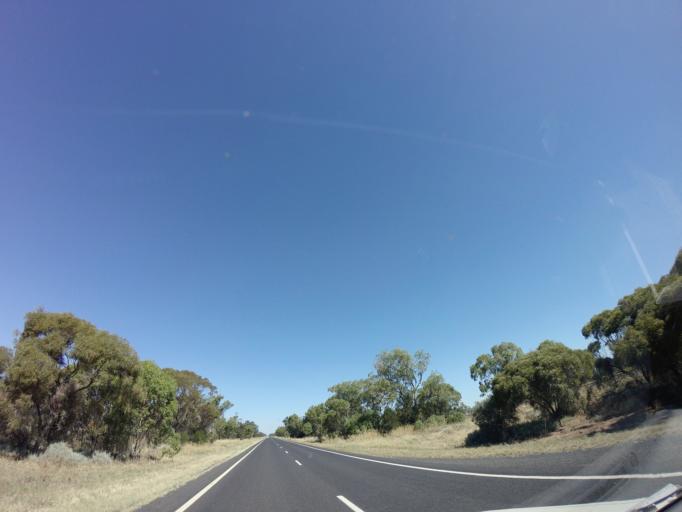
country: AU
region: New South Wales
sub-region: Bogan
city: Nyngan
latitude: -31.7839
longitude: 147.6153
